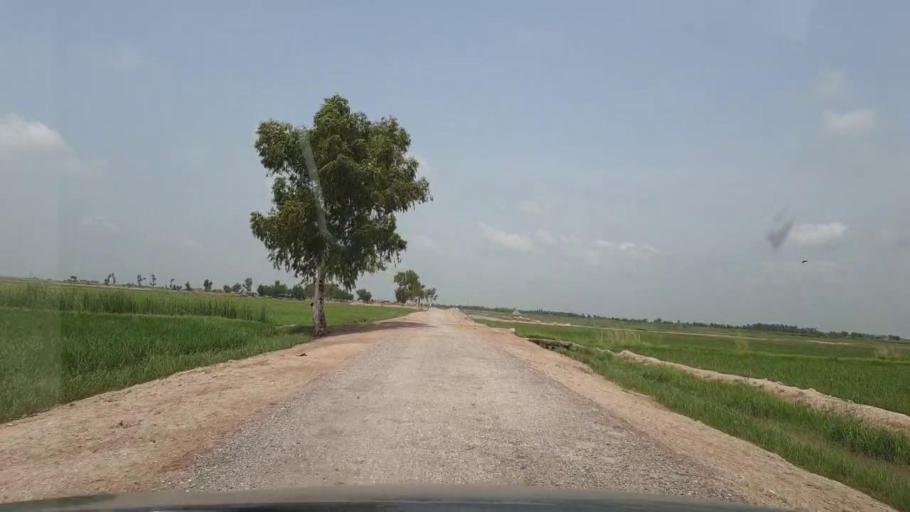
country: PK
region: Sindh
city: Ratodero
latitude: 27.9150
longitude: 68.3138
